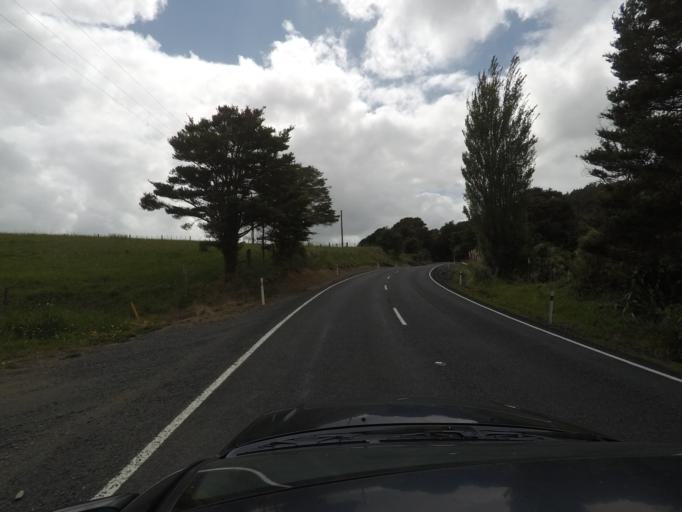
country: NZ
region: Auckland
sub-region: Auckland
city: Parakai
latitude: -36.5029
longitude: 174.5156
